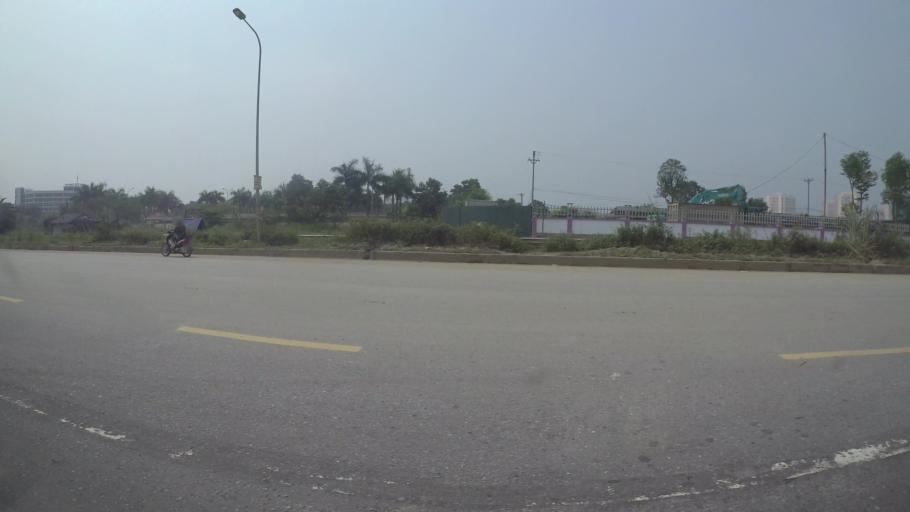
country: VN
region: Ha Noi
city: Lien Quan
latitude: 20.9904
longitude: 105.5179
